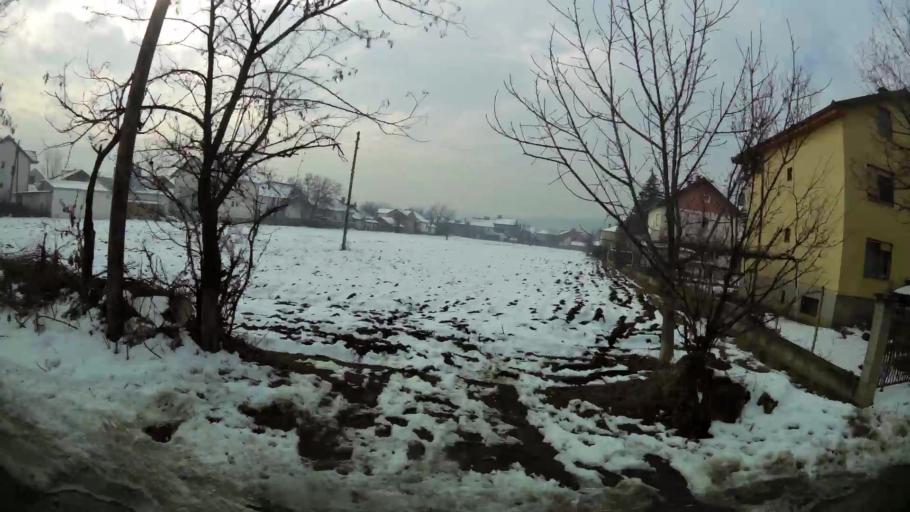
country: MK
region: Saraj
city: Saraj
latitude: 42.0263
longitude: 21.3545
